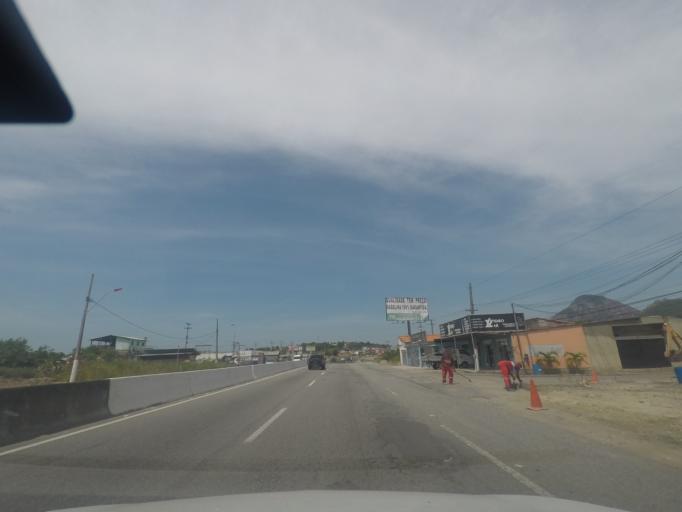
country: BR
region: Rio de Janeiro
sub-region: Marica
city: Marica
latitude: -22.9290
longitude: -42.8706
